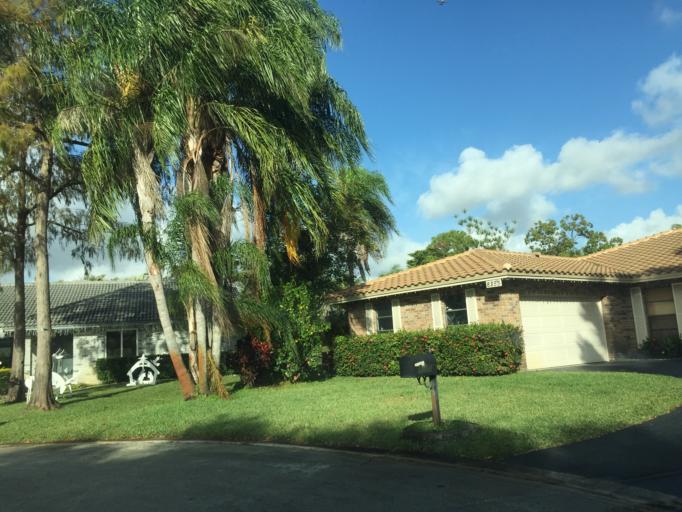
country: US
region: Florida
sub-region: Broward County
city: North Lauderdale
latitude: 26.2382
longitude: -80.2361
